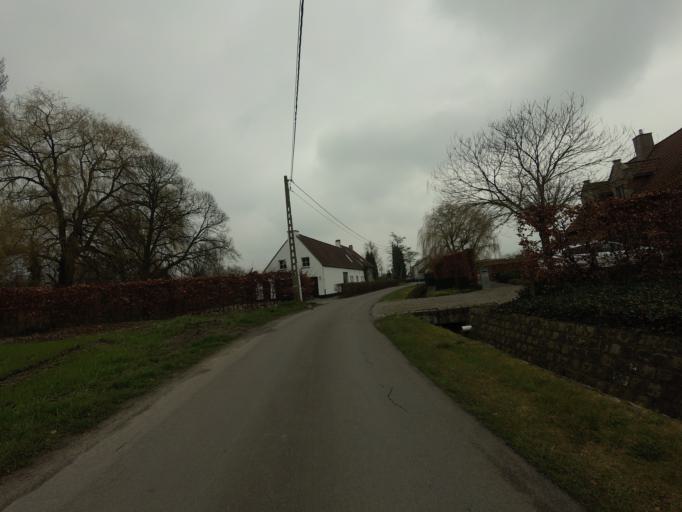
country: BE
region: Flanders
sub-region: Provincie Antwerpen
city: Putte
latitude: 51.0706
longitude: 4.5890
